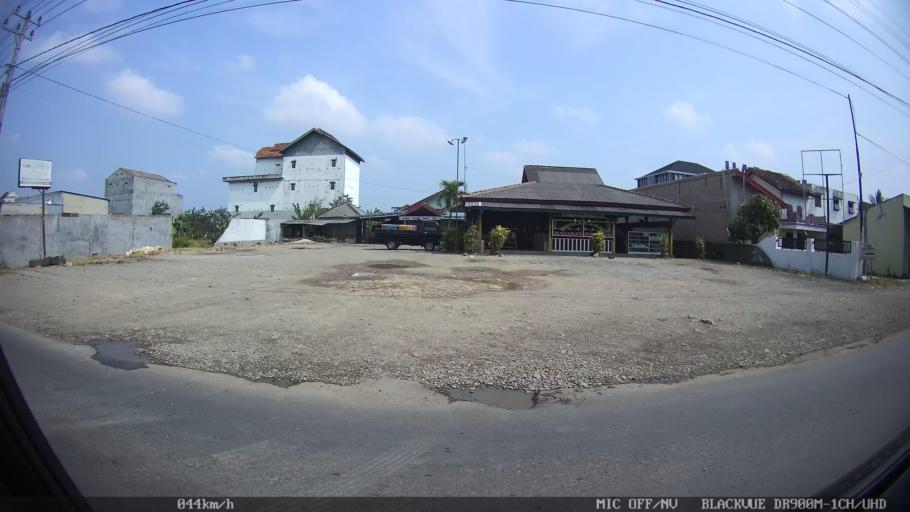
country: ID
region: Lampung
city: Gadingrejo
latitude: -5.3751
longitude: 105.0399
